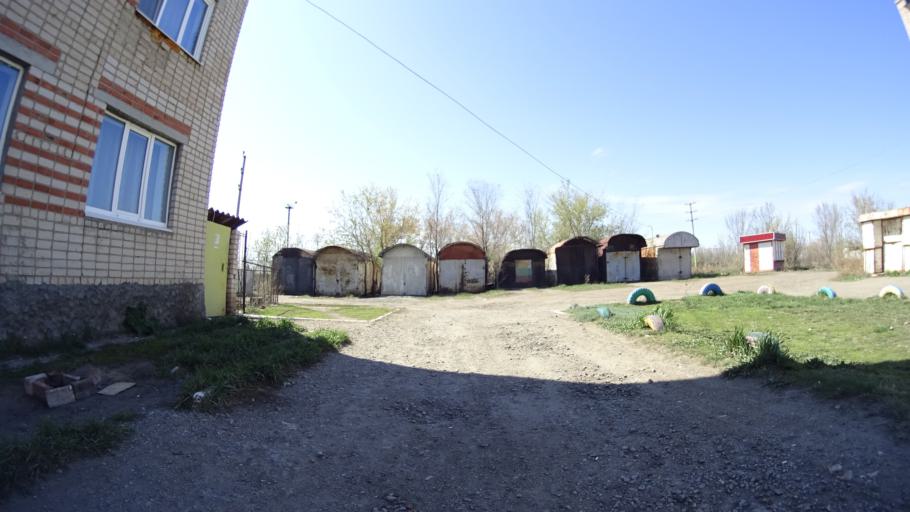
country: RU
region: Chelyabinsk
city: Troitsk
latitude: 54.1357
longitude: 61.5638
